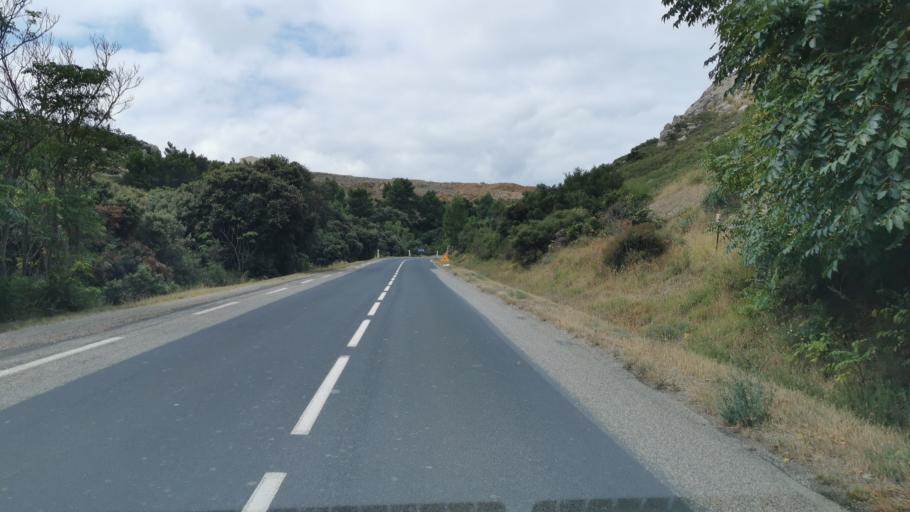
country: FR
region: Languedoc-Roussillon
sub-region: Departement de l'Aude
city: Bizanet
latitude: 43.1682
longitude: 2.9098
